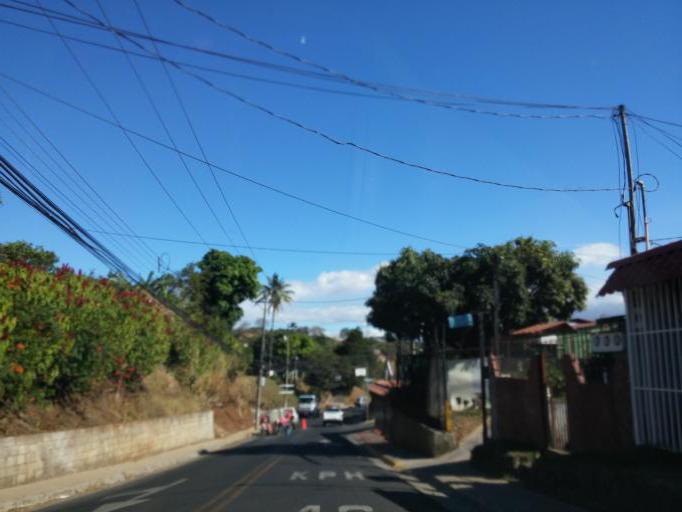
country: CR
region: Alajuela
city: Alajuela
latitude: 10.0215
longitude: -84.1881
